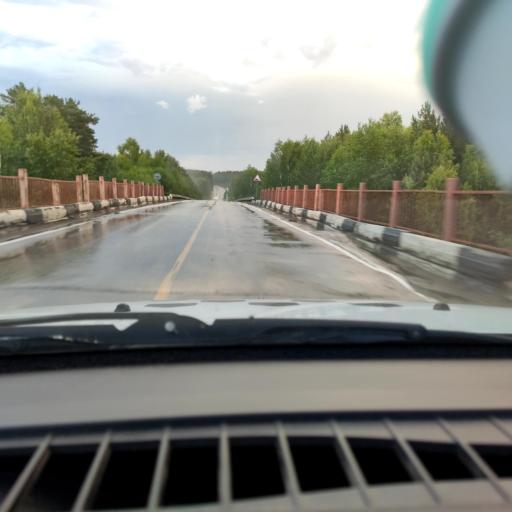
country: RU
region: Chelyabinsk
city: Kyshtym
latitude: 55.7317
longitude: 60.5254
